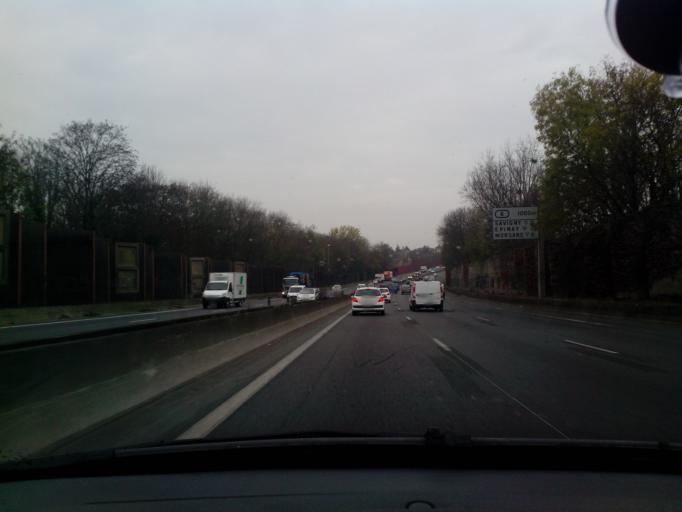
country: FR
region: Ile-de-France
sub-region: Departement de l'Essonne
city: Morsang-sur-Orge
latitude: 48.6687
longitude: 2.3528
